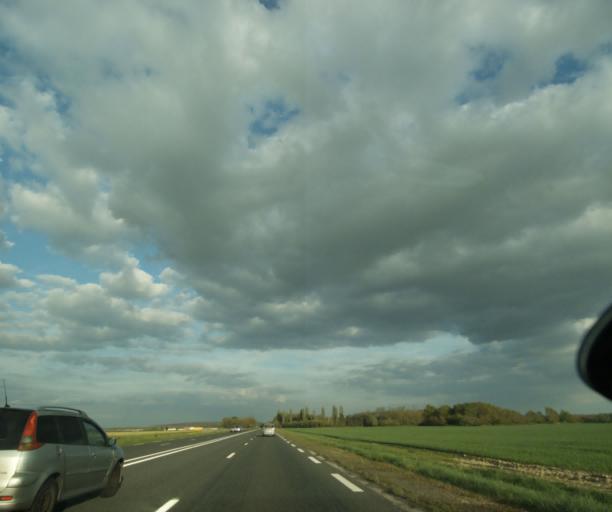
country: FR
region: Ile-de-France
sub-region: Departement de Seine-et-Marne
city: Perthes
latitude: 48.4597
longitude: 2.5754
